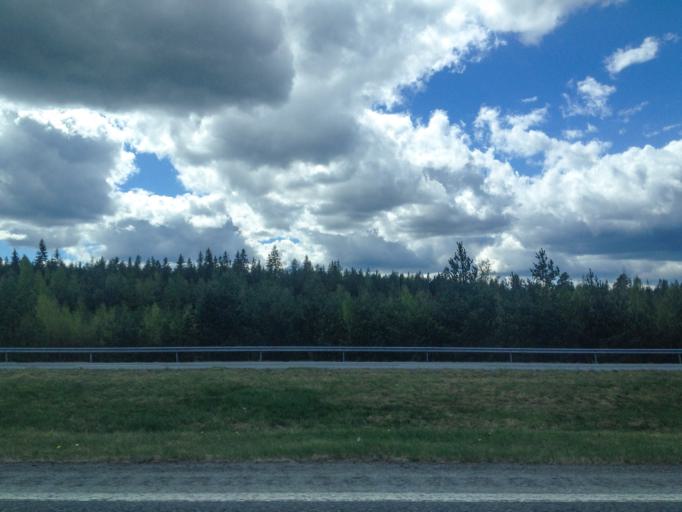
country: FI
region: Haeme
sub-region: Haemeenlinna
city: Kalvola
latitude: 61.1238
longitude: 24.1199
